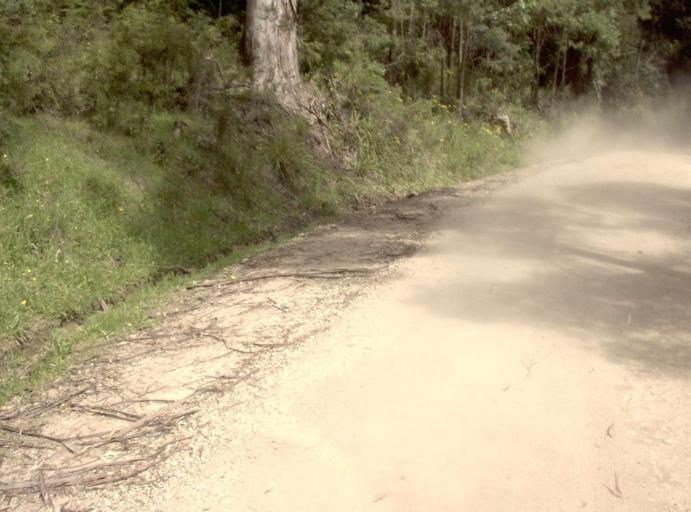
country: AU
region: Victoria
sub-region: East Gippsland
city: Lakes Entrance
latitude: -37.6228
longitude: 148.6976
